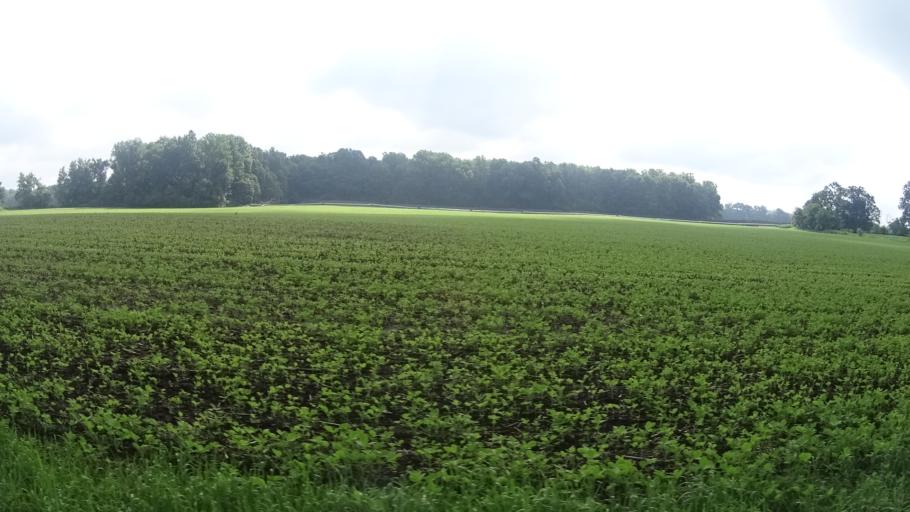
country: US
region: Ohio
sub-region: Huron County
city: Wakeman
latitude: 41.3165
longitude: -82.4662
